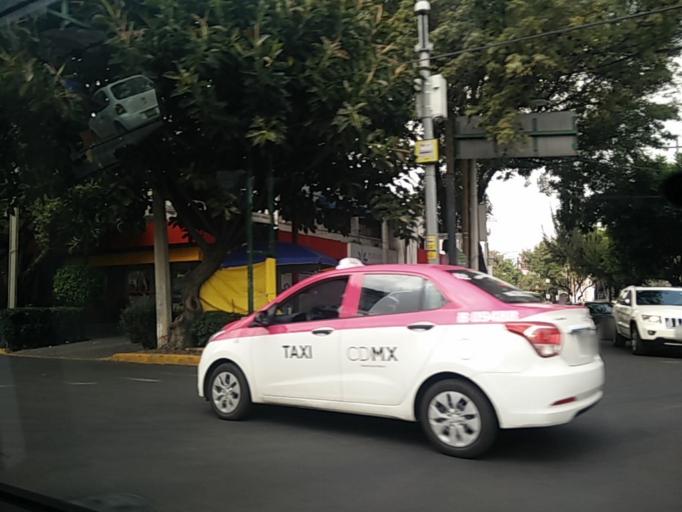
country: MX
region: Mexico City
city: Benito Juarez
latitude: 19.4013
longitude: -99.1622
